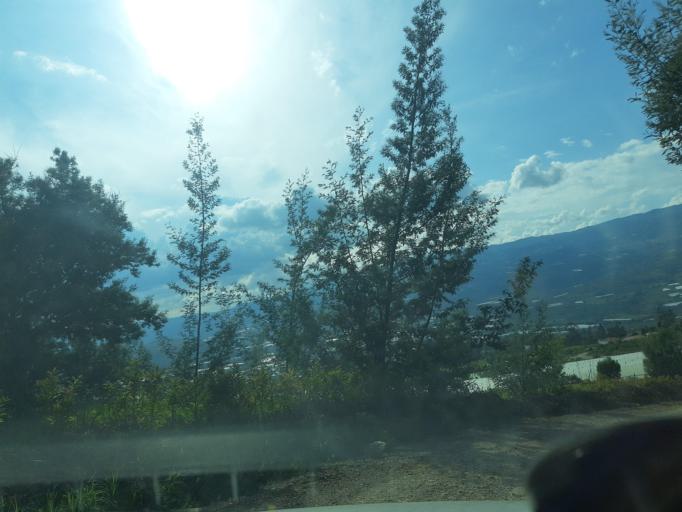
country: CO
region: Boyaca
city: Villa de Leiva
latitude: 5.6668
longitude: -73.5552
